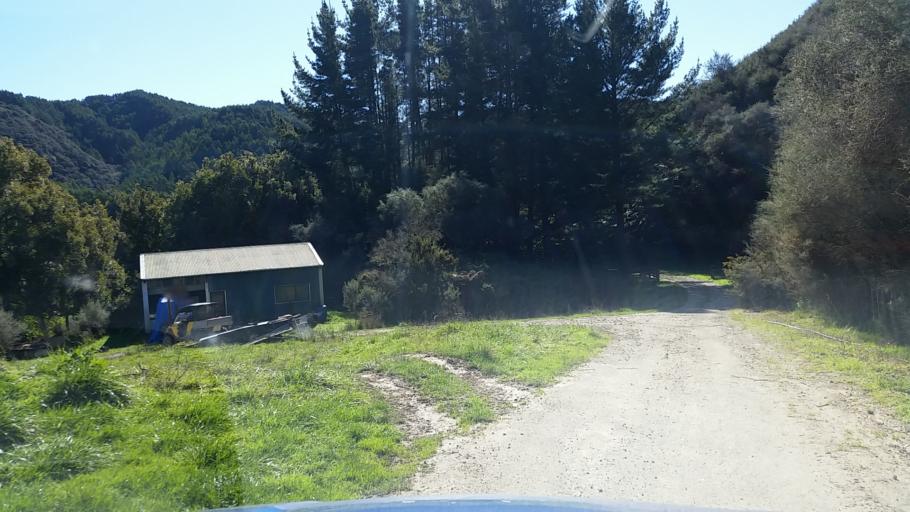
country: NZ
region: Manawatu-Wanganui
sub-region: Wanganui District
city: Wanganui
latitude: -39.6621
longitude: 174.8761
